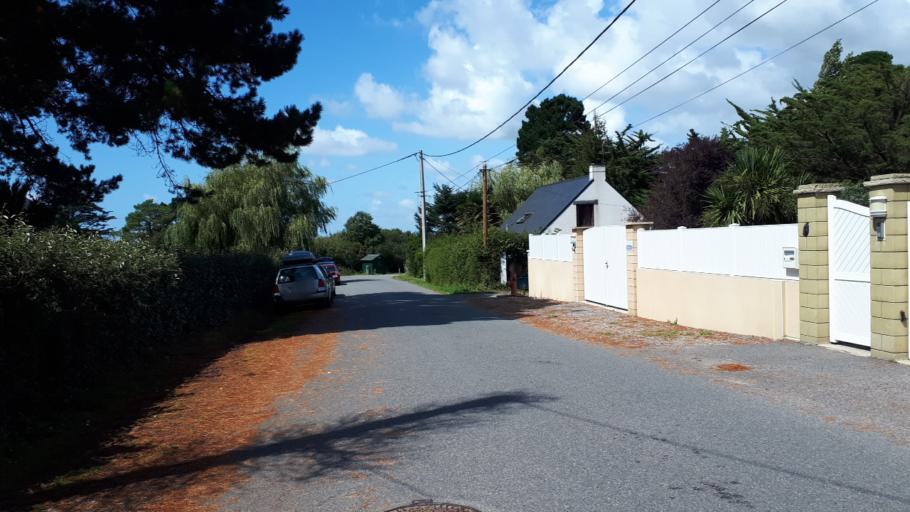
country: FR
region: Brittany
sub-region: Departement du Morbihan
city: Penestin
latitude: 47.4944
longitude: -2.4941
